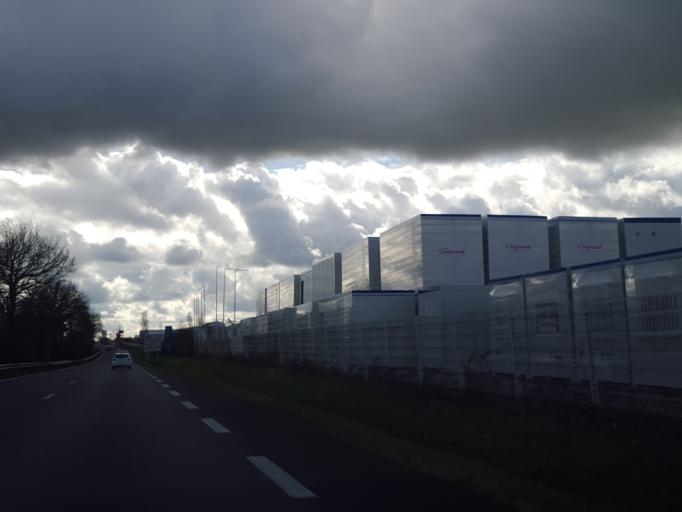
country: FR
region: Pays de la Loire
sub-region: Departement de la Vendee
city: Mouilleron-le-Captif
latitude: 46.7211
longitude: -1.4301
